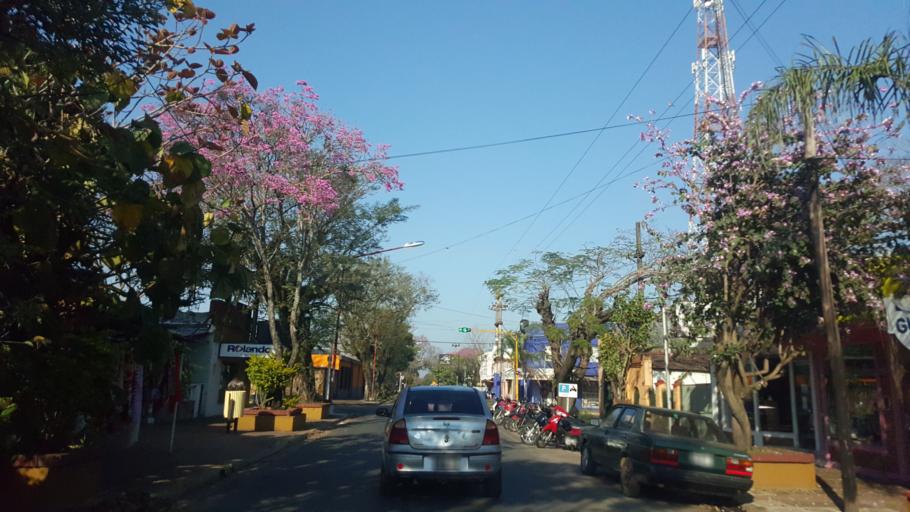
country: AR
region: Corrientes
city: Ituzaingo
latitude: -27.5875
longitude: -56.6905
